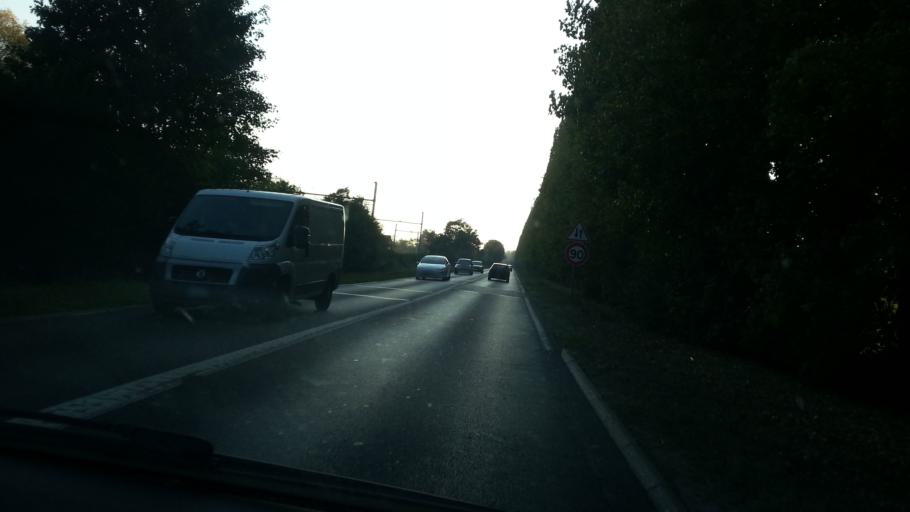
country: FR
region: Picardie
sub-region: Departement de l'Oise
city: Rieux
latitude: 49.2966
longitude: 2.5168
